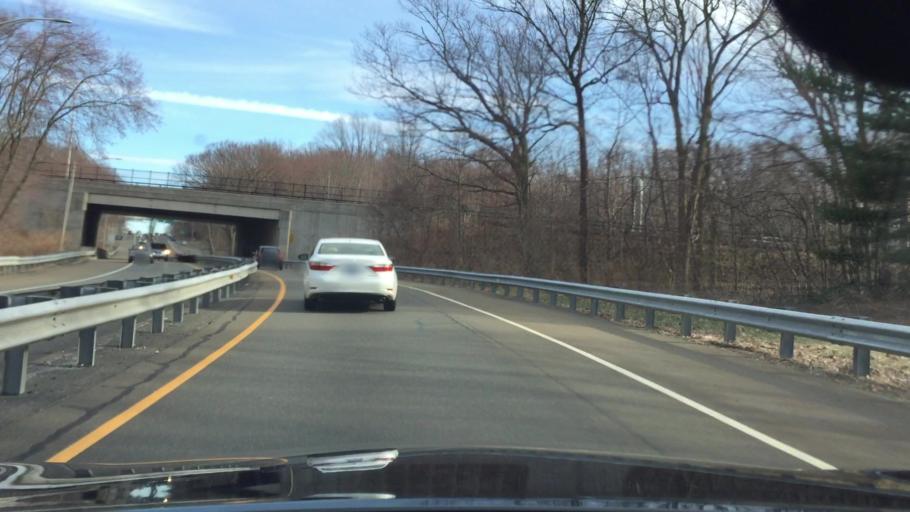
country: US
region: Connecticut
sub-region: New Haven County
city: City of Milford (balance)
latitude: 41.2477
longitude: -73.0860
